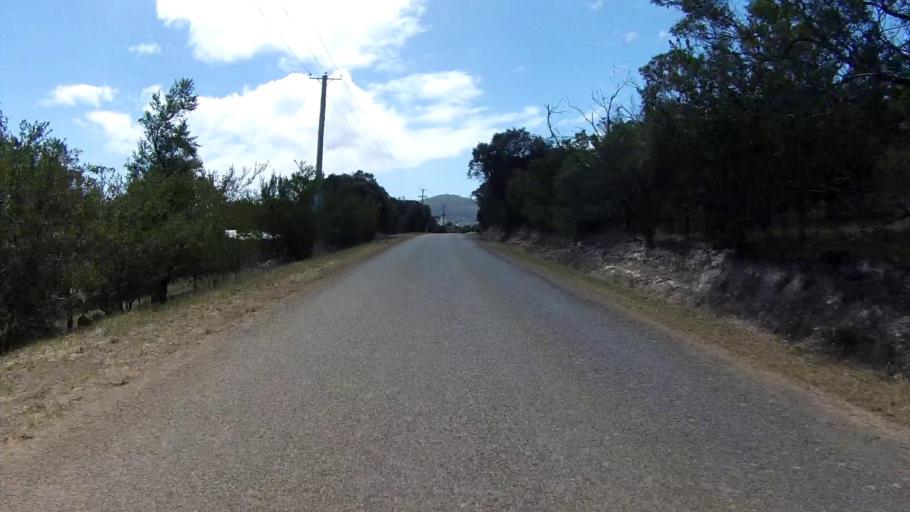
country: AU
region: Tasmania
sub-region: Clarence
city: Lauderdale
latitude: -42.9287
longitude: 147.4657
